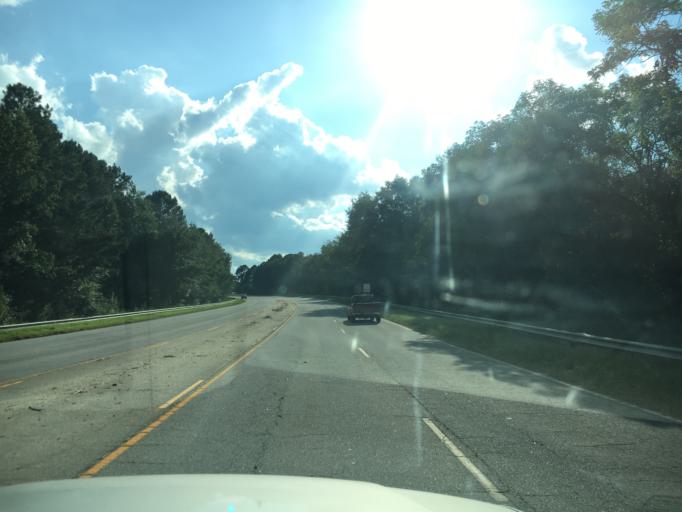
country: US
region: South Carolina
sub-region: Greenwood County
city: Ninety Six
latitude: 34.2727
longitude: -82.0738
